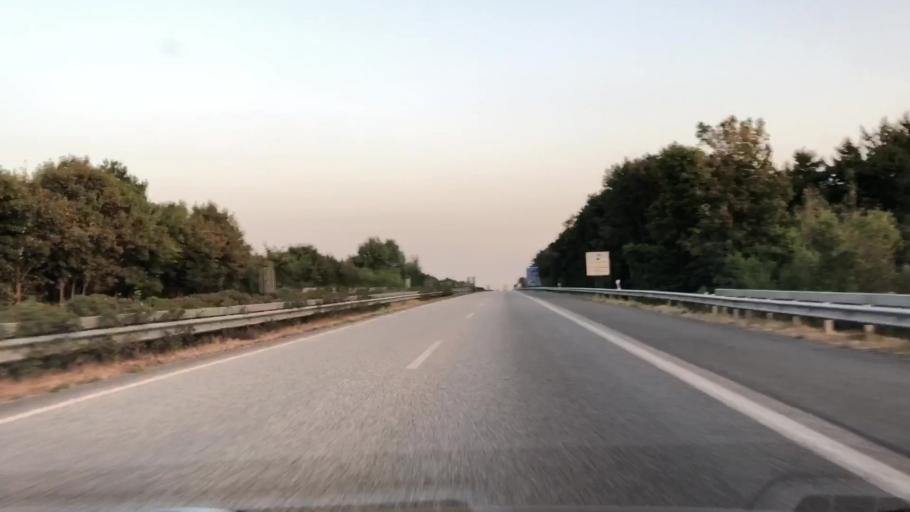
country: DE
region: Schleswig-Holstein
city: Jarplund-Weding
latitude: 54.7443
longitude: 9.3798
